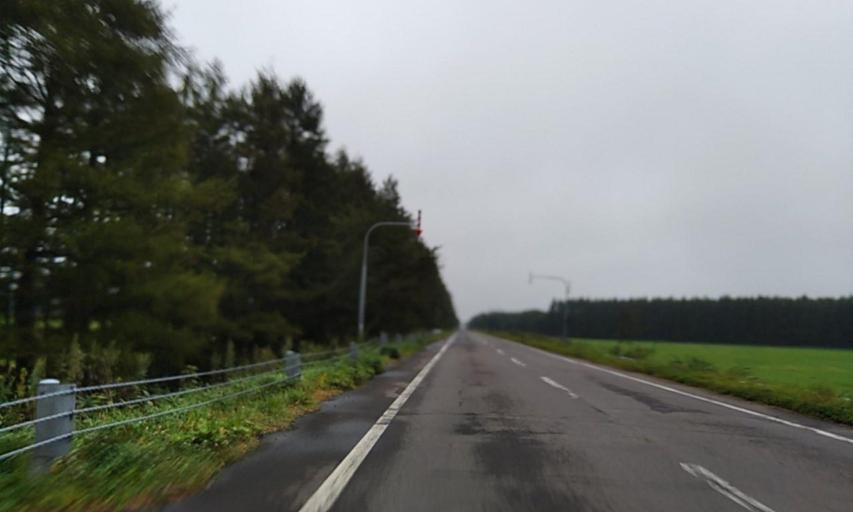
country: JP
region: Hokkaido
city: Shibetsu
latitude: 43.5228
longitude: 144.6887
